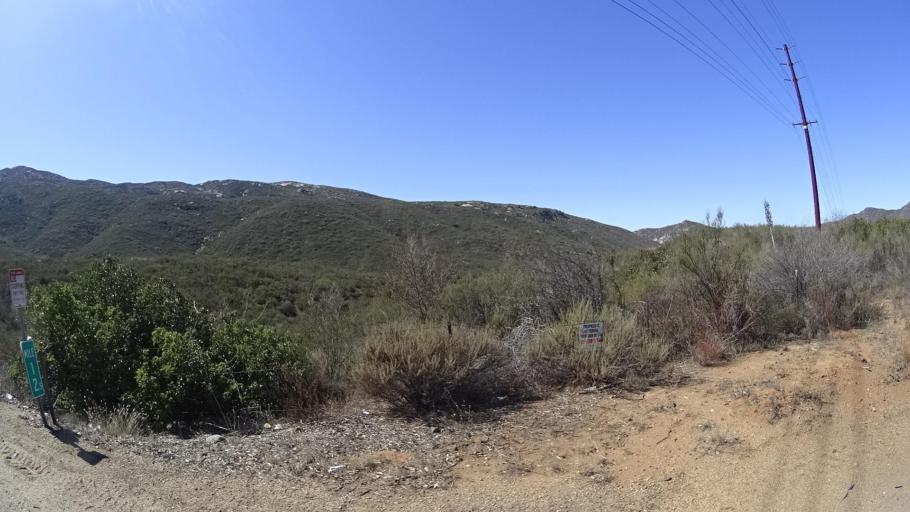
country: US
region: California
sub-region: San Diego County
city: Alpine
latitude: 32.7917
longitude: -116.7394
